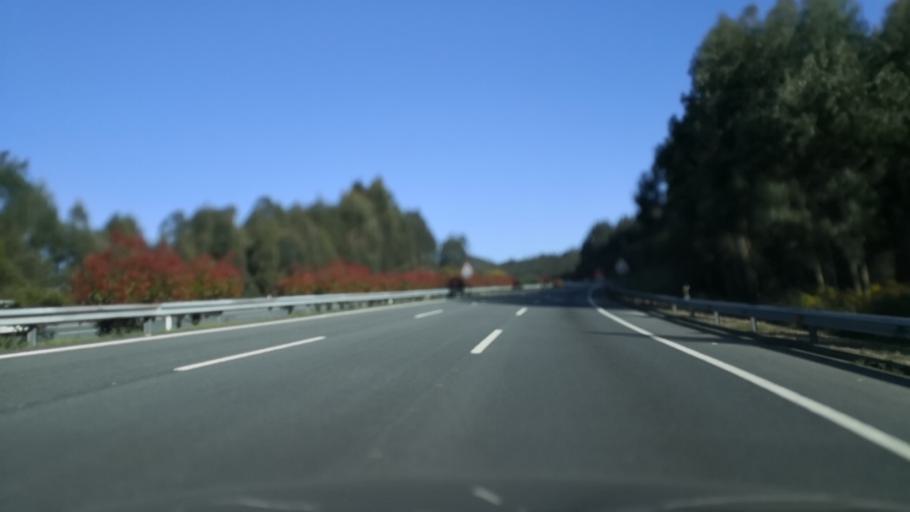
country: ES
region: Galicia
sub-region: Provincia da Coruna
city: Irixoa
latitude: 43.2343
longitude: -8.0798
